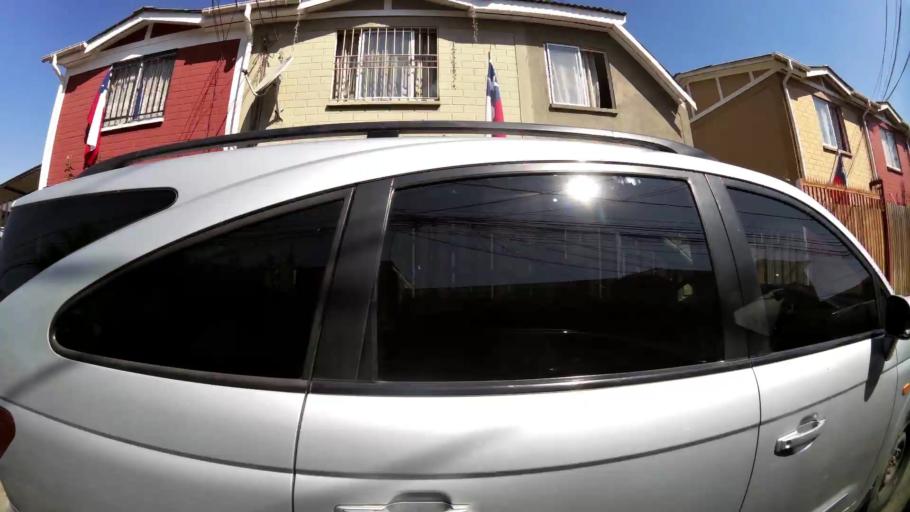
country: CL
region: Santiago Metropolitan
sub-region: Provincia de Santiago
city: Lo Prado
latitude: -33.3515
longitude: -70.7344
